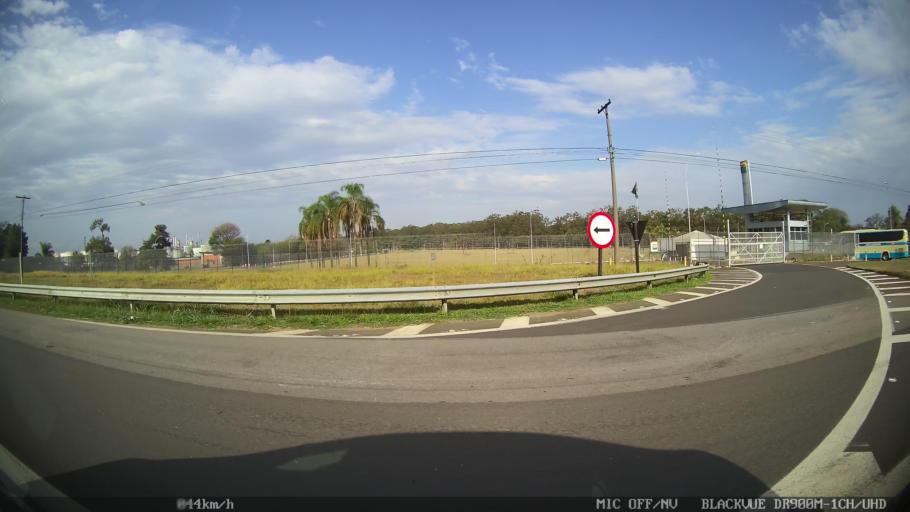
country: BR
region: Sao Paulo
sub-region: Paulinia
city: Paulinia
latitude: -22.7291
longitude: -47.1480
